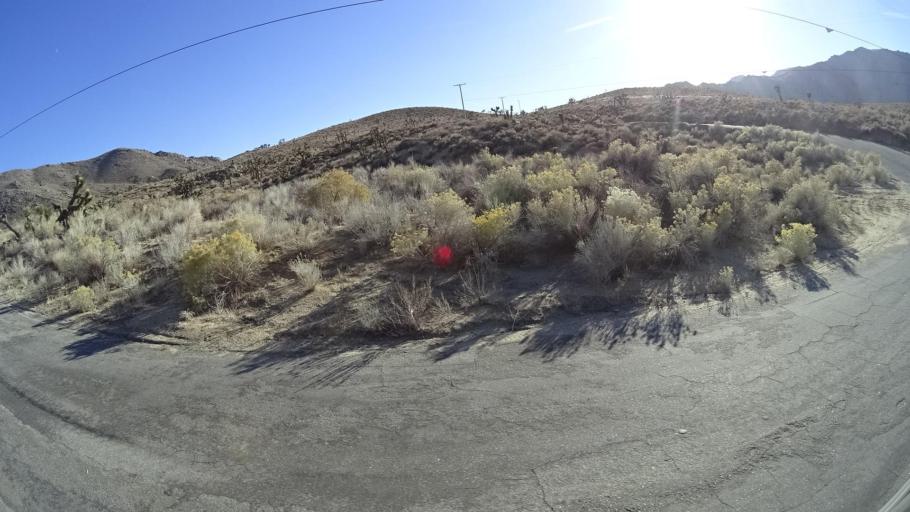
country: US
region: California
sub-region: Kern County
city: Weldon
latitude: 35.5247
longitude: -118.2027
